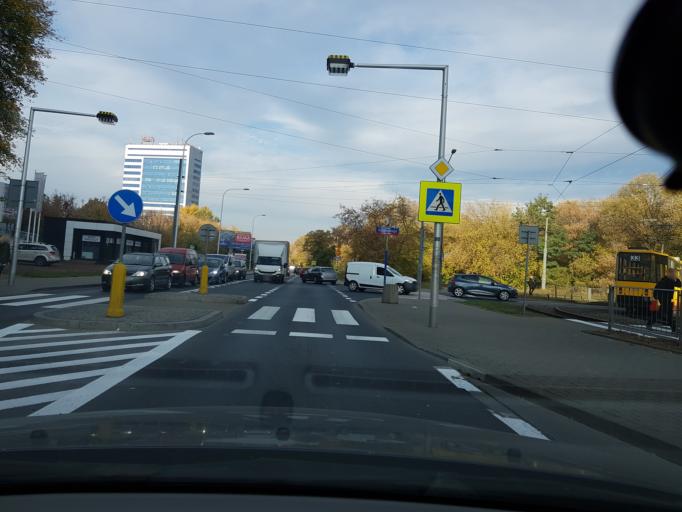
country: PL
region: Masovian Voivodeship
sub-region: Warszawa
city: Bielany
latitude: 52.2820
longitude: 20.9208
